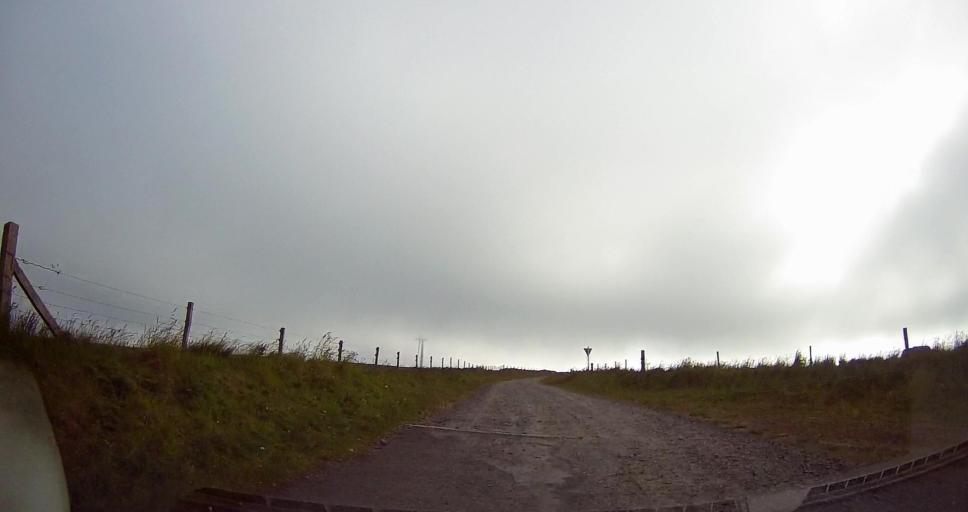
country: GB
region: Scotland
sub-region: Orkney Islands
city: Stromness
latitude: 59.1192
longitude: -3.1385
